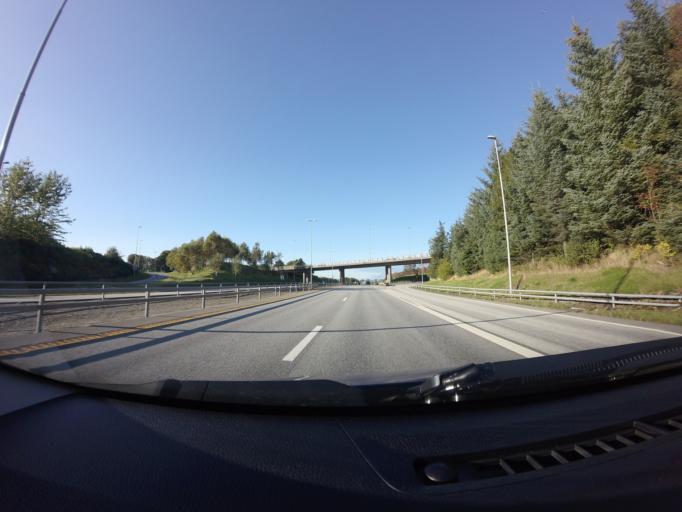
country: NO
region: Rogaland
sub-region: Sandnes
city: Sandnes
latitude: 58.8564
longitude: 5.7119
